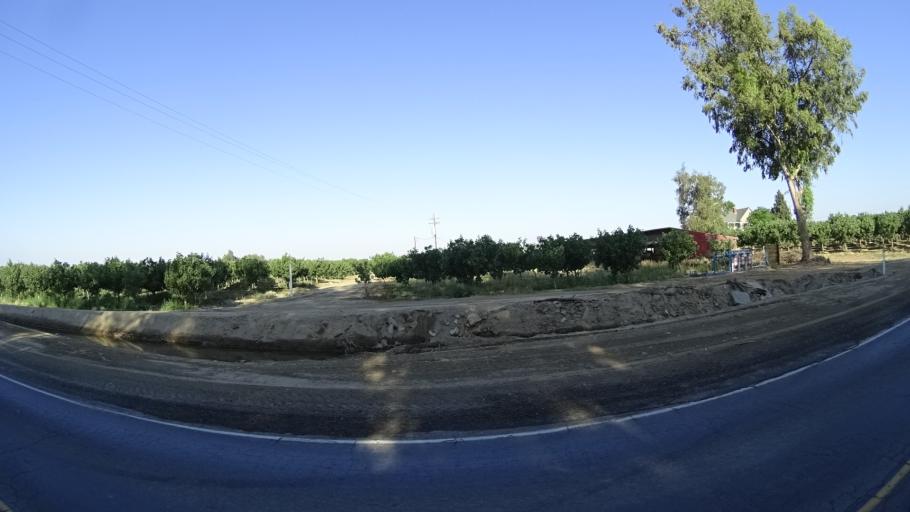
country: US
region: California
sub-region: Kings County
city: Armona
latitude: 36.2682
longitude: -119.7090
